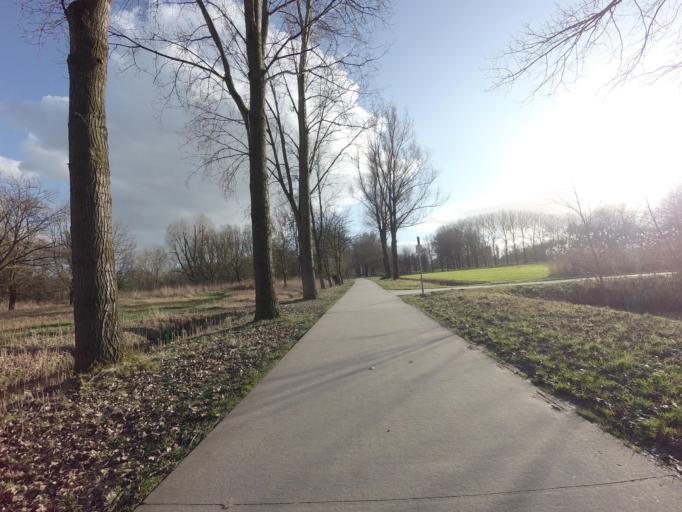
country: NL
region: Utrecht
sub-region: Gemeente Nieuwegein
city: Nieuwegein
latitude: 52.0200
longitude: 5.0848
